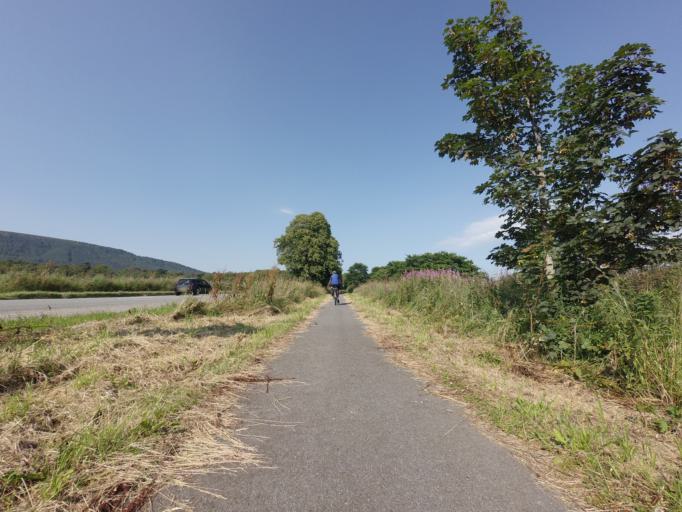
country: GB
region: Scotland
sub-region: Highland
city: Evanton
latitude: 57.6704
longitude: -4.3231
